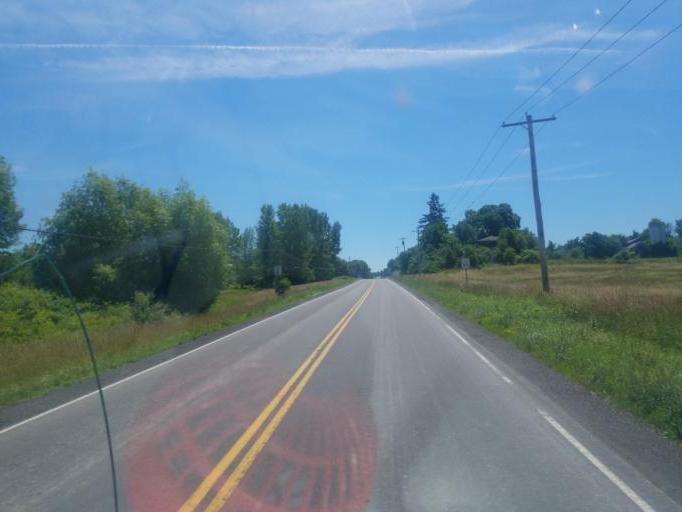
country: US
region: New York
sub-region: Yates County
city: Penn Yan
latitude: 42.6315
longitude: -76.9994
